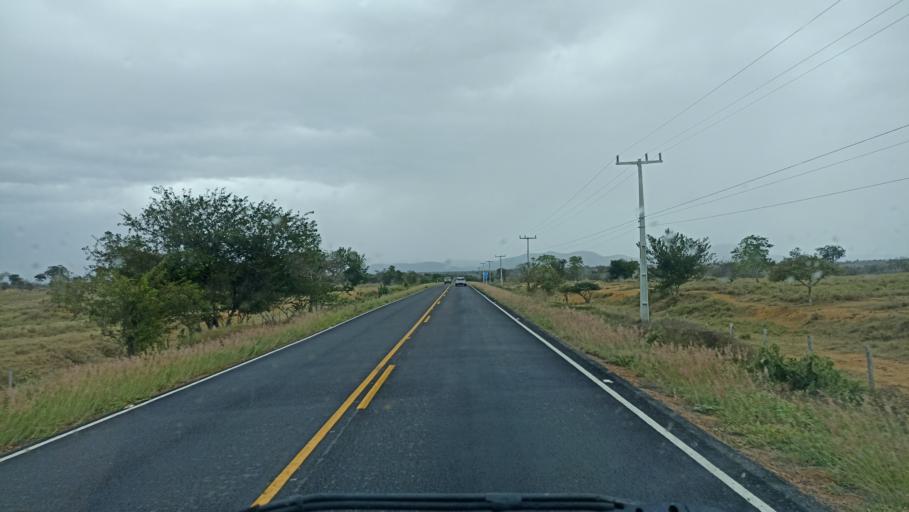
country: BR
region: Bahia
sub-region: Maracas
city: Maracas
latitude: -13.0371
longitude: -40.6949
